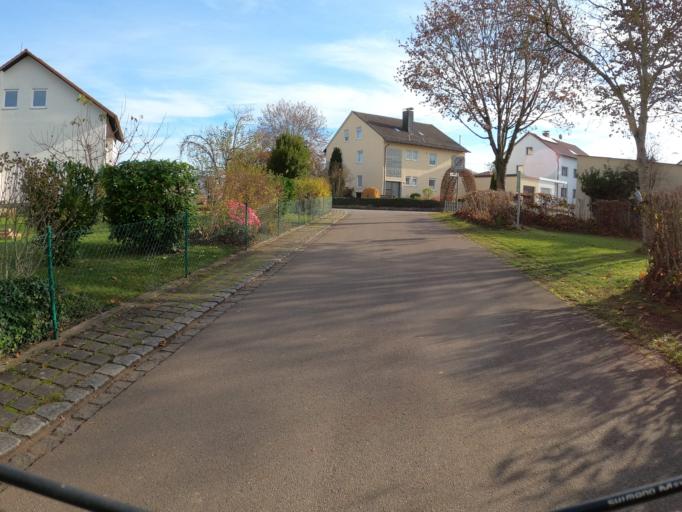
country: DE
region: Bavaria
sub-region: Swabia
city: Leipheim
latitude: 48.3997
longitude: 10.1973
